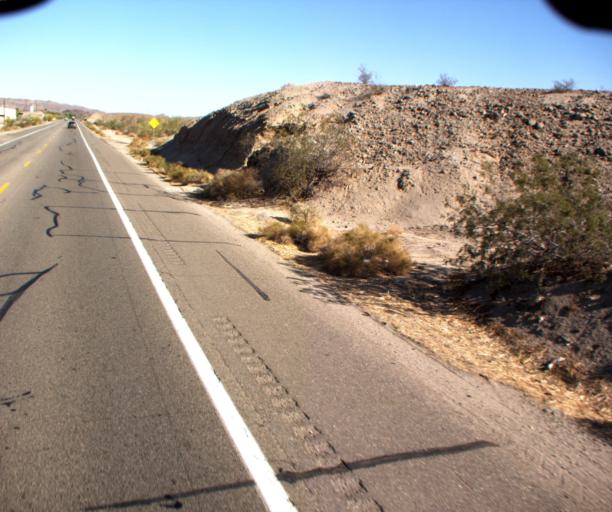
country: US
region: Arizona
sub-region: Yuma County
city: Fortuna Foothills
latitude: 32.7313
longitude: -114.4227
